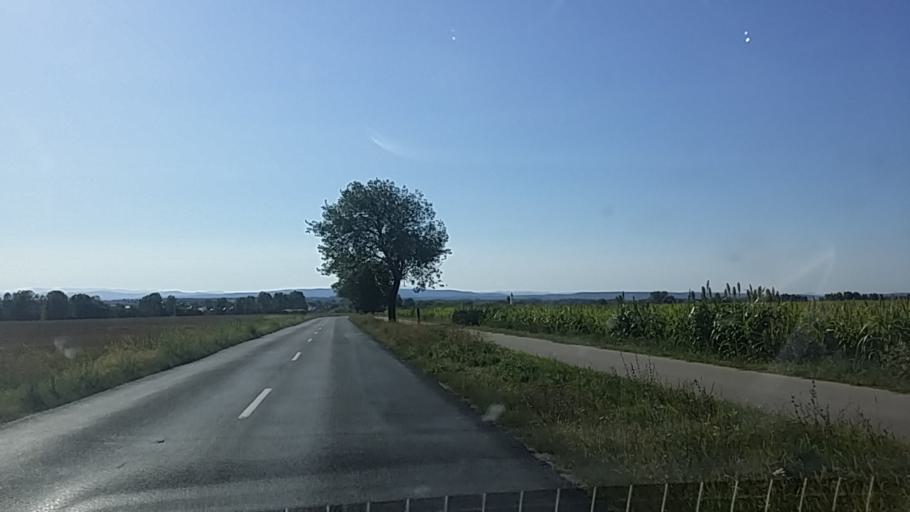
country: HU
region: Gyor-Moson-Sopron
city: Fertod
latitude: 47.6172
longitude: 16.8146
